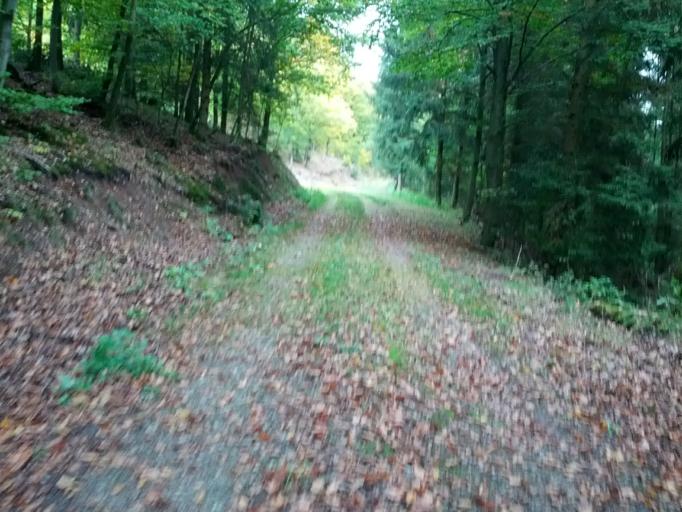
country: DE
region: Thuringia
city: Eisenach
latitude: 50.9696
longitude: 10.2902
